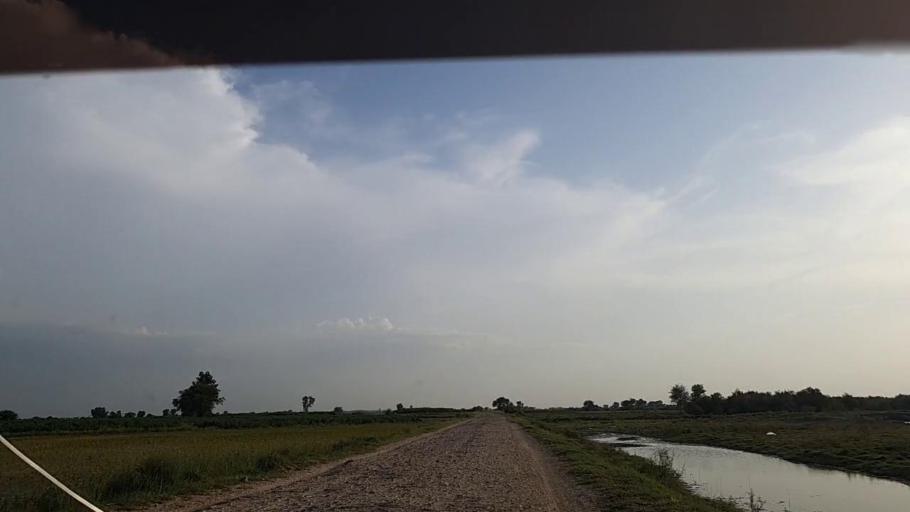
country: PK
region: Sindh
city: Khanpur
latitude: 27.8067
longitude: 69.3182
